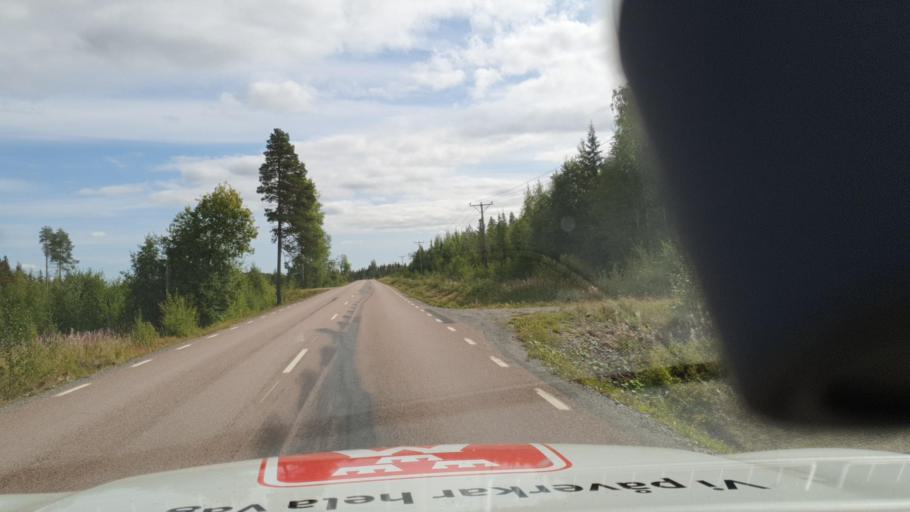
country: SE
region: Jaemtland
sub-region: Stroemsunds Kommun
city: Stroemsund
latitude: 63.8143
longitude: 15.6475
